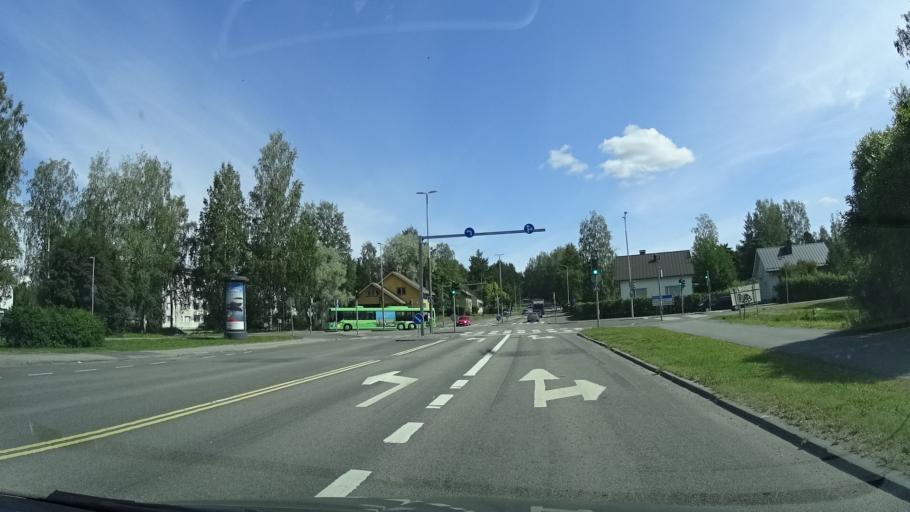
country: FI
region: Central Finland
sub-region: Jyvaeskylae
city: Jyvaeskylae
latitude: 62.2455
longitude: 25.7271
